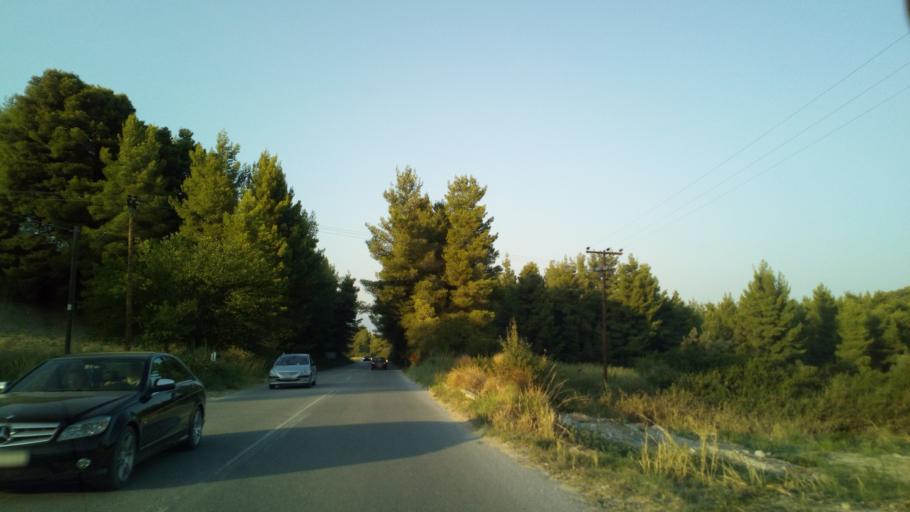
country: GR
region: Central Macedonia
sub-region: Nomos Chalkidikis
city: Pefkochori
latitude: 39.9536
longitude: 23.6719
